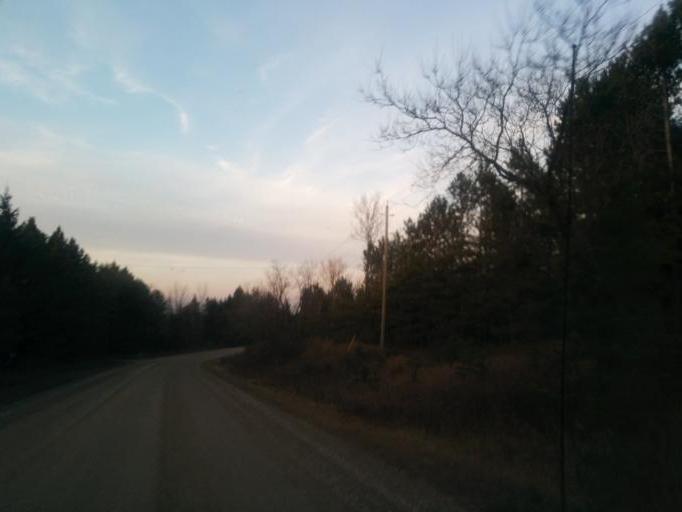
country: CA
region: Ontario
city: Orangeville
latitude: 43.9675
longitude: -79.9767
